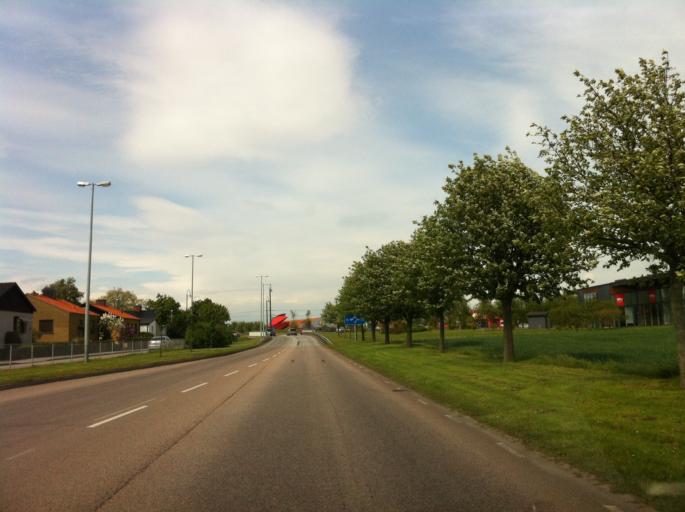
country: SE
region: Skane
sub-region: Landskrona
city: Landskrona
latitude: 55.8773
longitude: 12.8532
